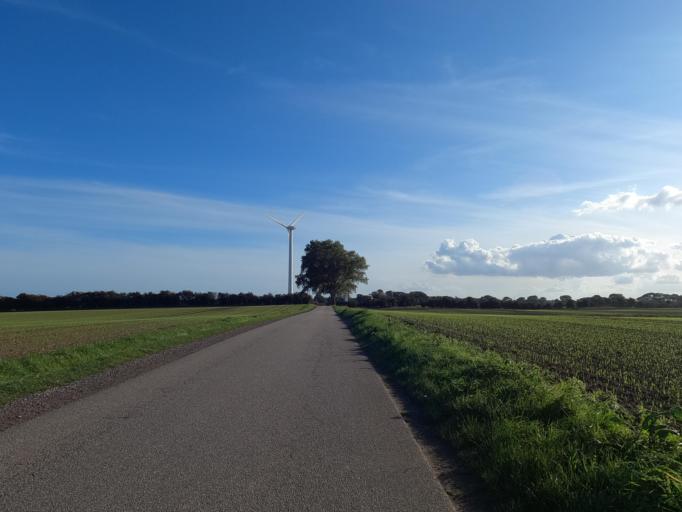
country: DE
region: Schleswig-Holstein
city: Neukirchen
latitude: 54.3417
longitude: 11.0504
